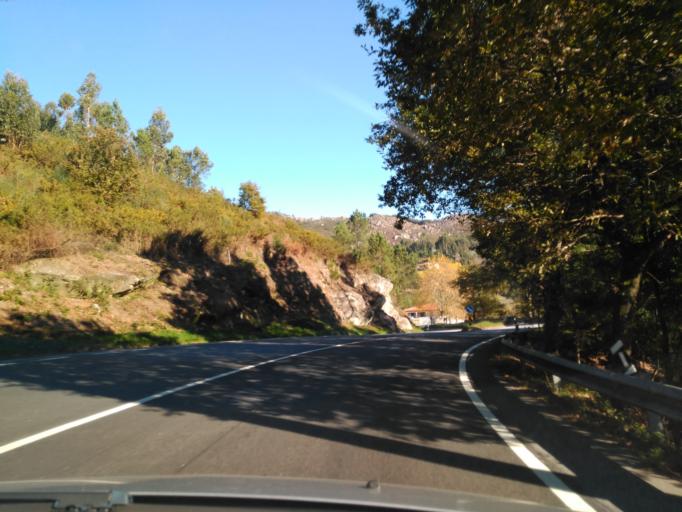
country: PT
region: Braga
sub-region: Povoa de Lanhoso
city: Povoa de Lanhoso
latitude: 41.6128
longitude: -8.2580
